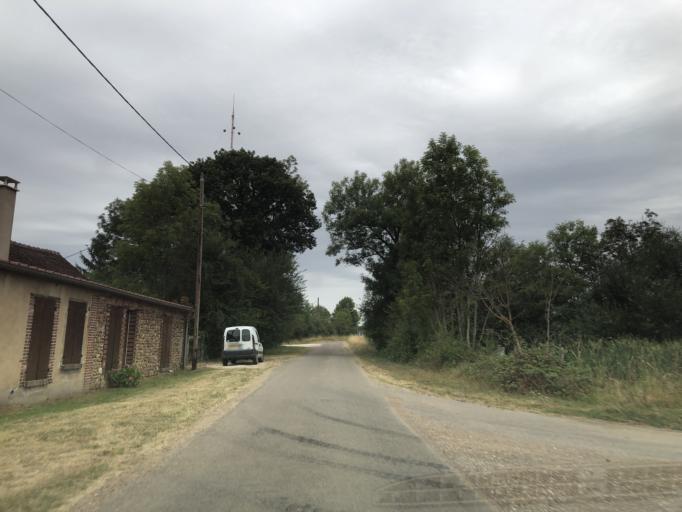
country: FR
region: Bourgogne
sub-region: Departement de l'Yonne
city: Aillant-sur-Tholon
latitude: 47.9177
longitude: 3.3121
